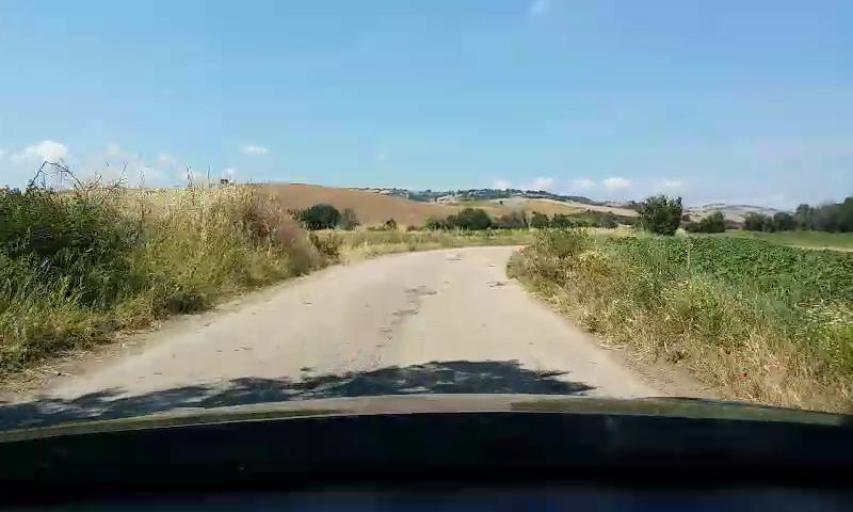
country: IT
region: Molise
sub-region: Provincia di Campobasso
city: Montecilfone
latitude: 41.9273
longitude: 14.8552
